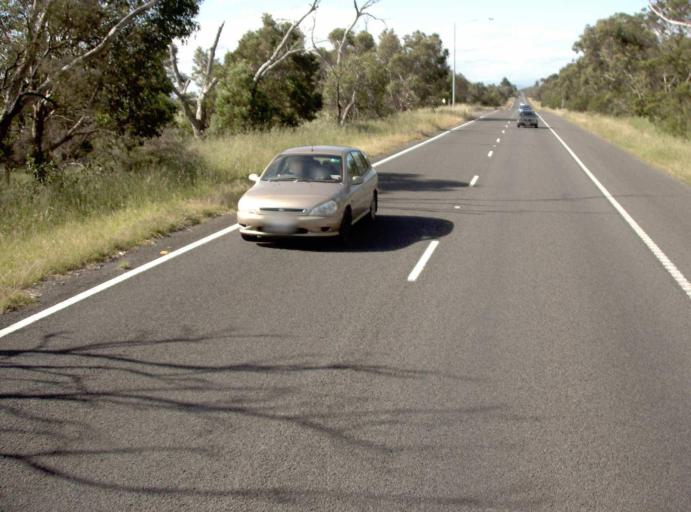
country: AU
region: Victoria
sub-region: Cardinia
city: Koo-Wee-Rup
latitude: -38.3104
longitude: 145.5416
